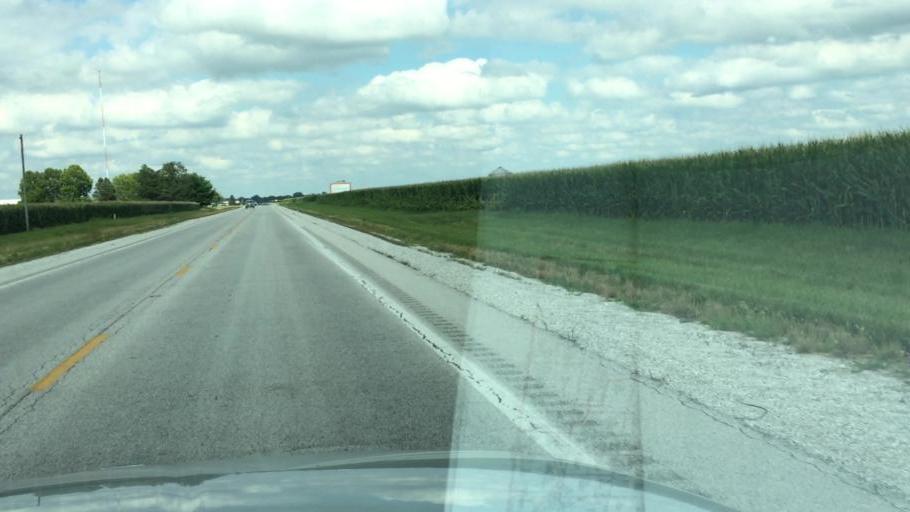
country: US
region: Illinois
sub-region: Hancock County
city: Carthage
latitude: 40.4066
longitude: -91.1763
